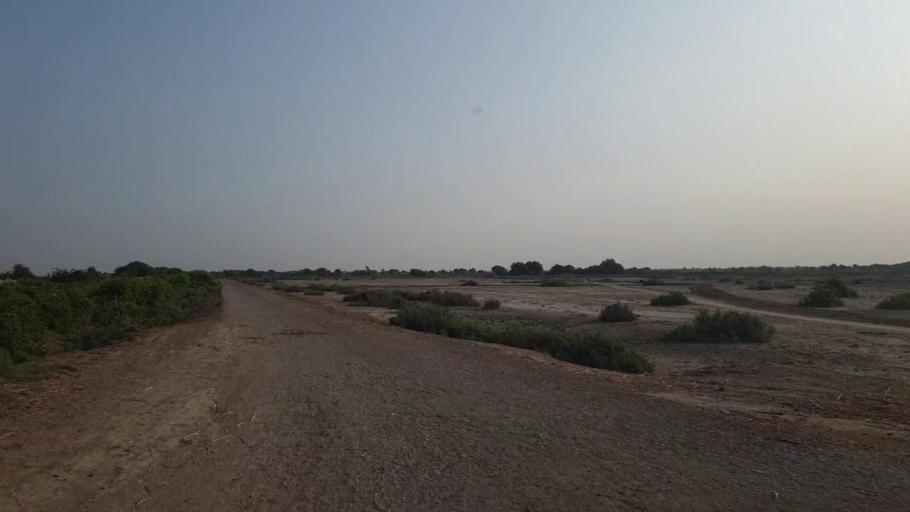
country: PK
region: Sindh
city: Rajo Khanani
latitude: 25.0093
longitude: 68.7859
